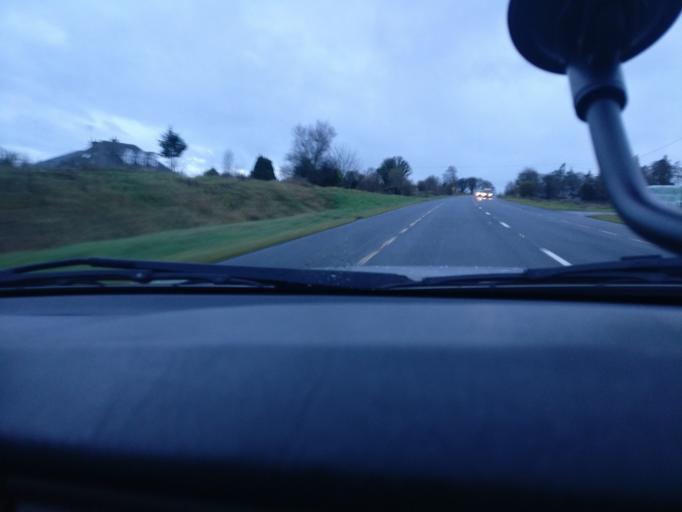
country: IE
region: Connaught
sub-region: County Galway
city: Ballinasloe
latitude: 53.2970
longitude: -8.3252
